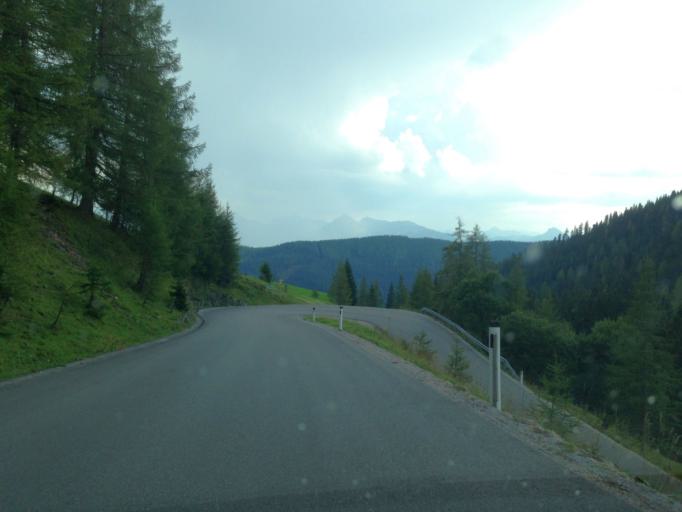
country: AT
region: Salzburg
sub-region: Politischer Bezirk Sankt Johann im Pongau
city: Filzmoos
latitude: 47.4440
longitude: 13.6073
